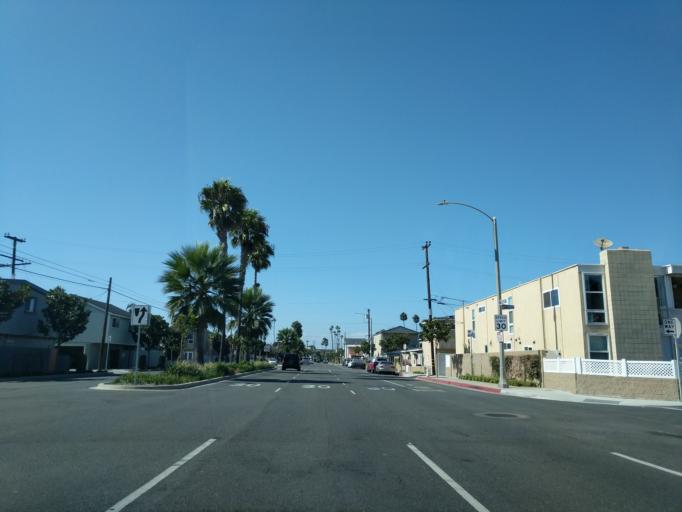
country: US
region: California
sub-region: Orange County
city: Newport Beach
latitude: 33.6192
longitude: -117.9365
